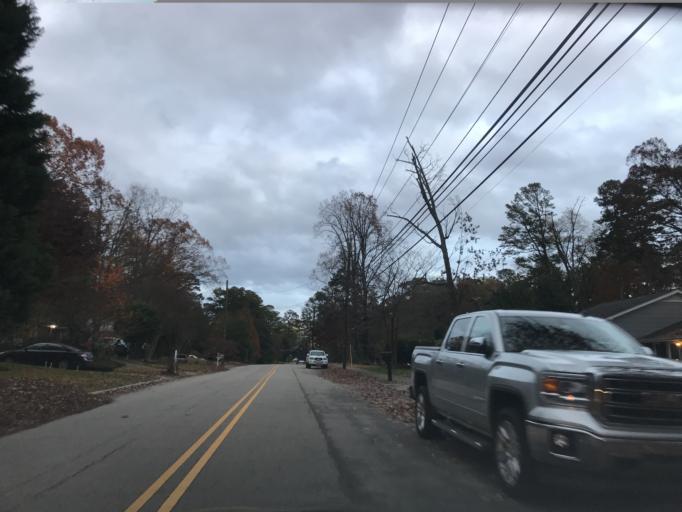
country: US
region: North Carolina
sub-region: Wake County
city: West Raleigh
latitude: 35.8368
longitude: -78.6495
